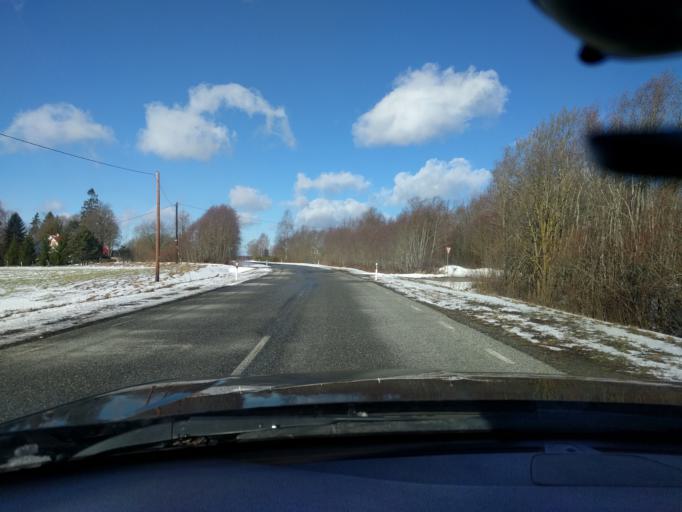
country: EE
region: Harju
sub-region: Raasiku vald
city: Raasiku
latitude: 59.3873
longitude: 25.1939
